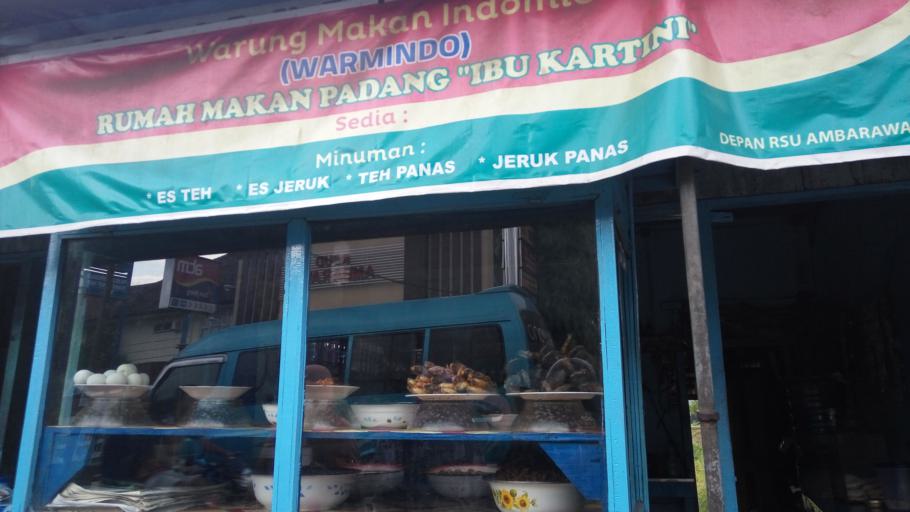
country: ID
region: Central Java
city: Ambarawa
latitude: -7.2676
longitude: 110.4086
